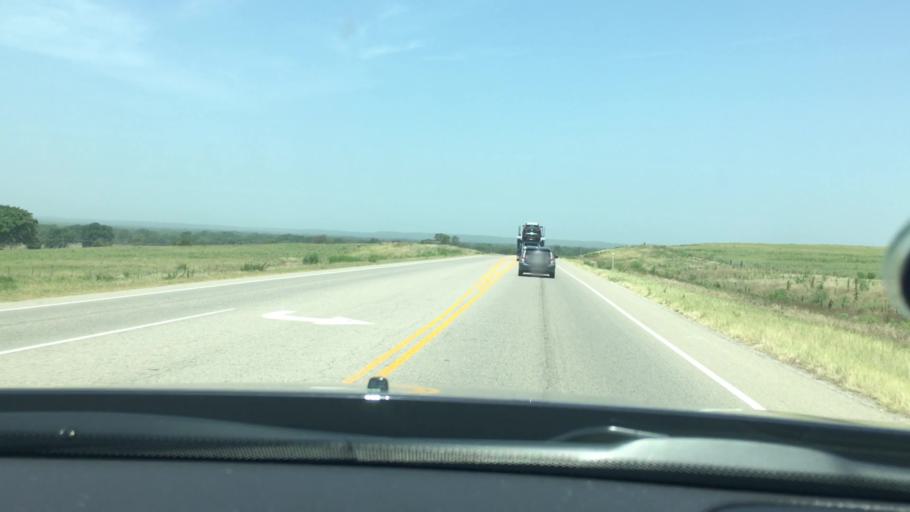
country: US
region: Oklahoma
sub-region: Pontotoc County
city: Ada
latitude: 34.6806
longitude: -96.5830
